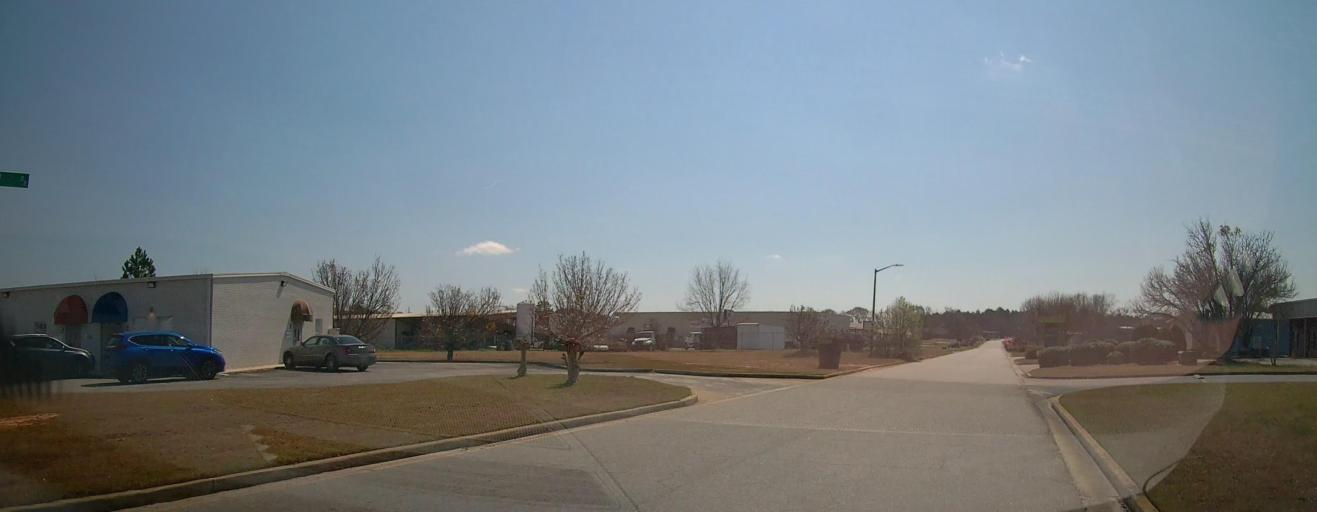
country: US
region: Georgia
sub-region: Houston County
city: Centerville
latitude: 32.6128
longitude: -83.6815
